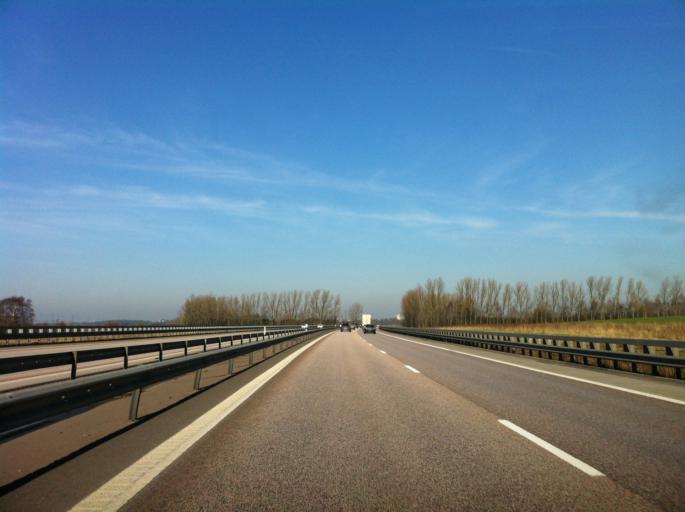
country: SE
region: Skane
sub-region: Helsingborg
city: Gantofta
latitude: 55.9845
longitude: 12.7826
